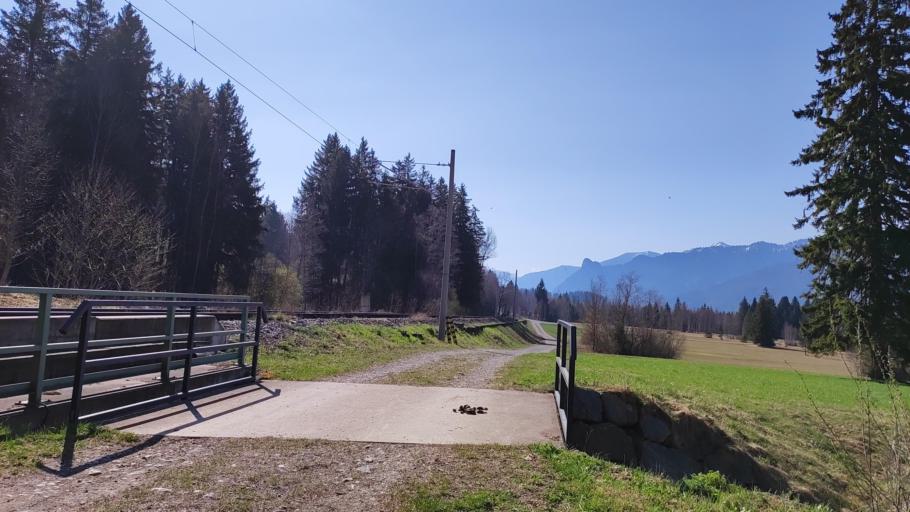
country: DE
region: Bavaria
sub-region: Upper Bavaria
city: Unterammergau
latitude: 47.6402
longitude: 11.0248
